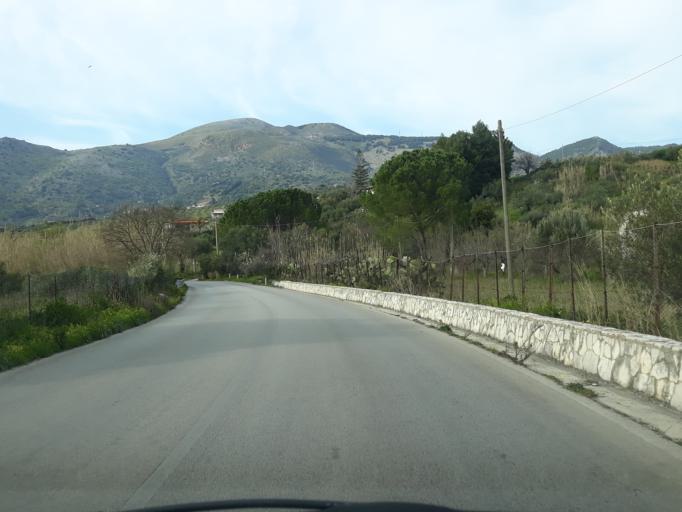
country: IT
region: Sicily
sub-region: Palermo
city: Giardinello
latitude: 38.0712
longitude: 13.1545
